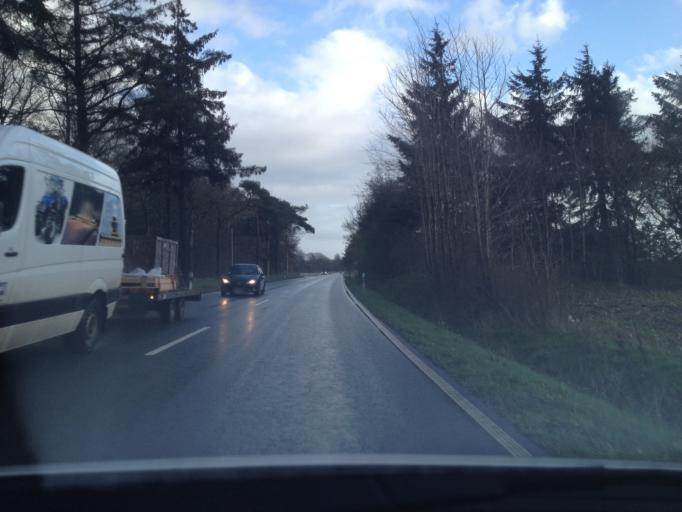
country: DE
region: Schleswig-Holstein
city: Tinningstedt
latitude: 54.7873
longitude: 8.9384
